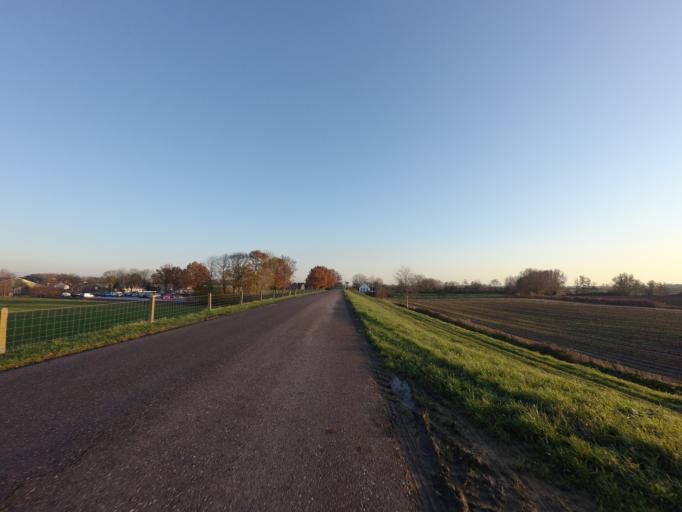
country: NL
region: Gelderland
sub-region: Gemeente Zaltbommel
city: Nederhemert-Noord
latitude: 51.7471
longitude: 5.1949
